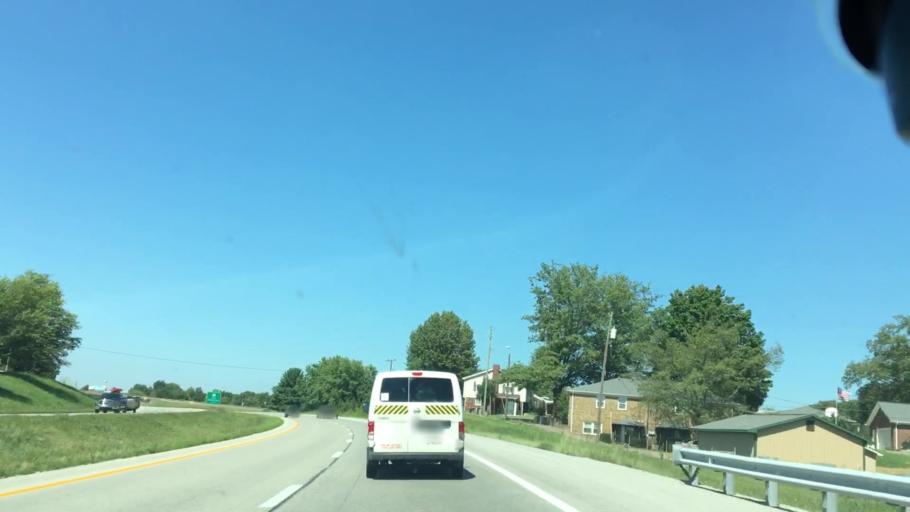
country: US
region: Kentucky
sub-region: Henderson County
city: Henderson
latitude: 37.8213
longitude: -87.5626
